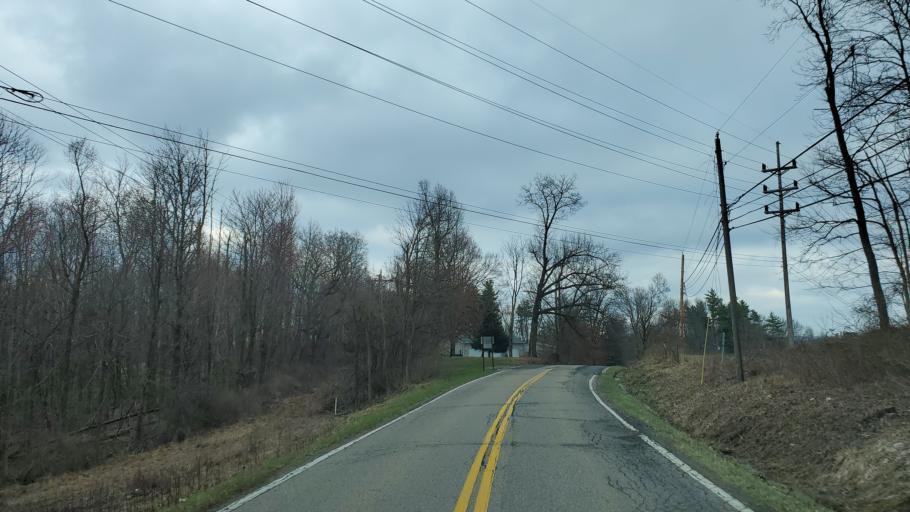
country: US
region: Ohio
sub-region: Licking County
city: Newark
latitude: 40.0302
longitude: -82.3710
